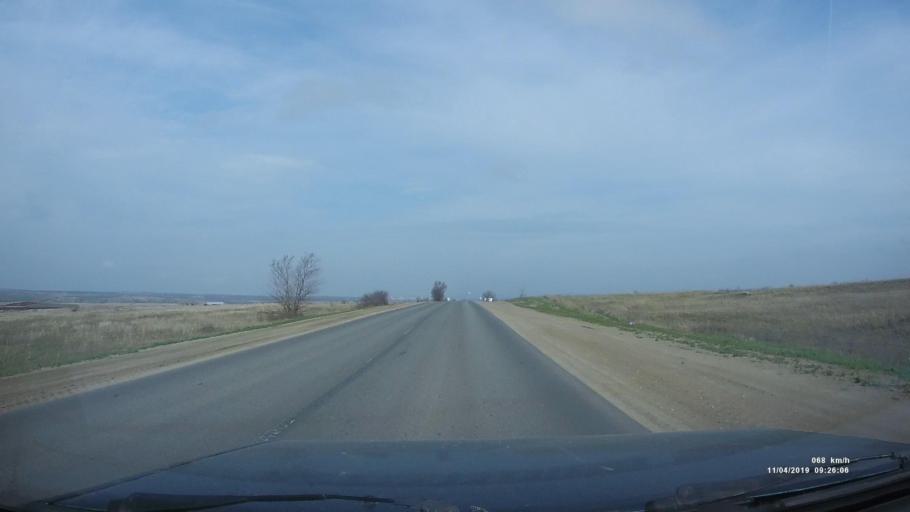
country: RU
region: Rostov
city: Staraya Stanitsa
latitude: 48.2614
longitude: 40.3663
